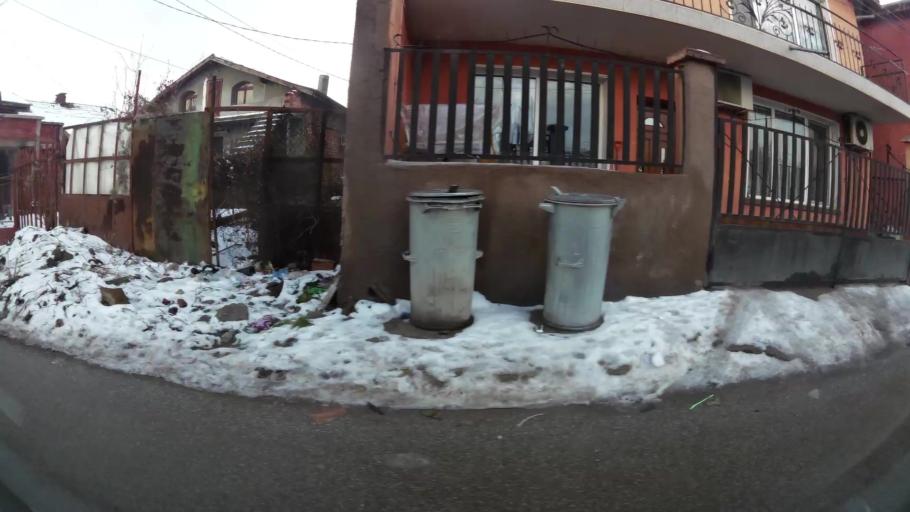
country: BG
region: Sofia-Capital
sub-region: Stolichna Obshtina
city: Sofia
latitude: 42.6969
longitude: 23.2664
